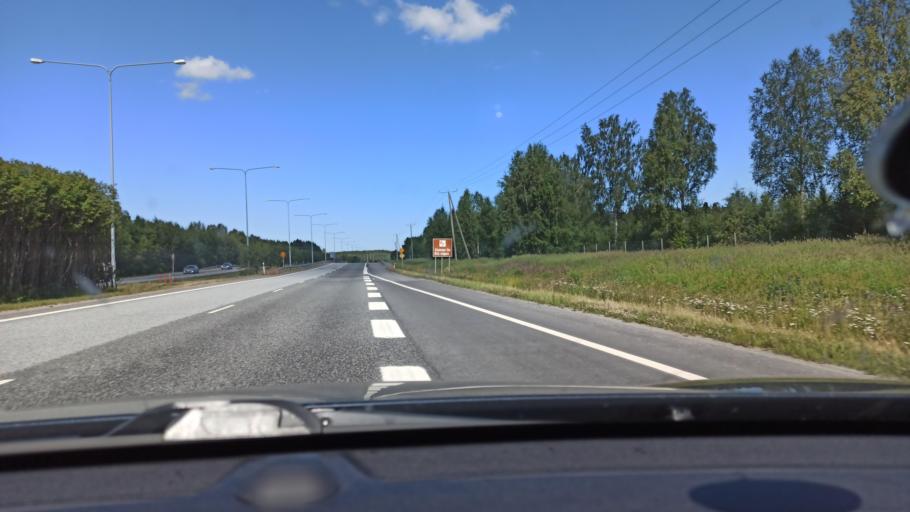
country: FI
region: Ostrobothnia
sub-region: Vaasa
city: Ristinummi
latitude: 63.0386
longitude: 21.7347
